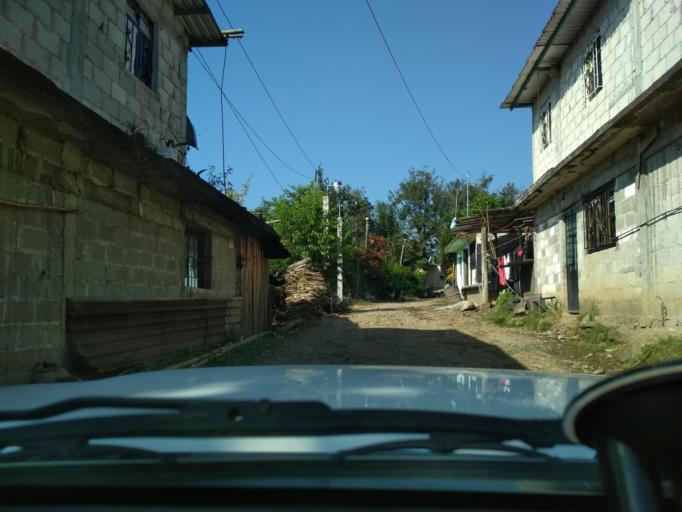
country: MX
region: Veracruz
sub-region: Chocaman
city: San Jose Neria
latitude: 18.9994
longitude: -97.0037
